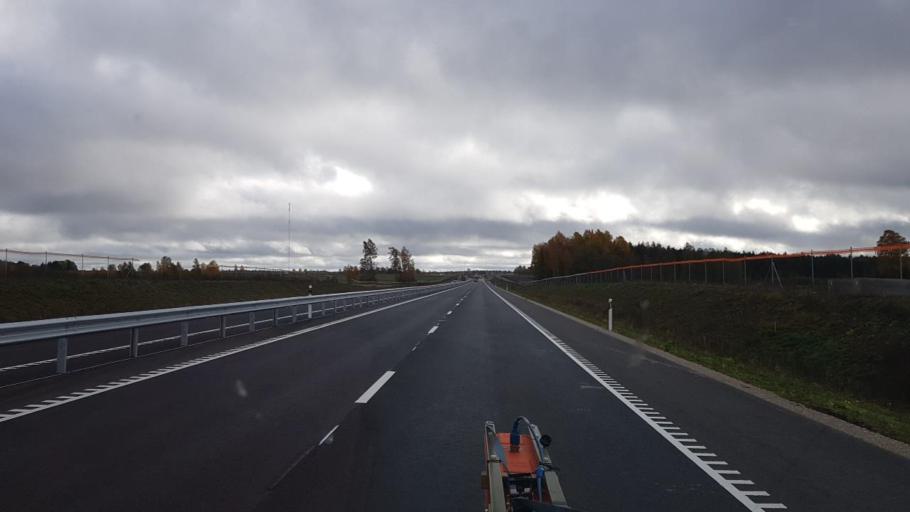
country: EE
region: Jaervamaa
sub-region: Paide linn
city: Paide
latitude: 59.0020
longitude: 25.5737
